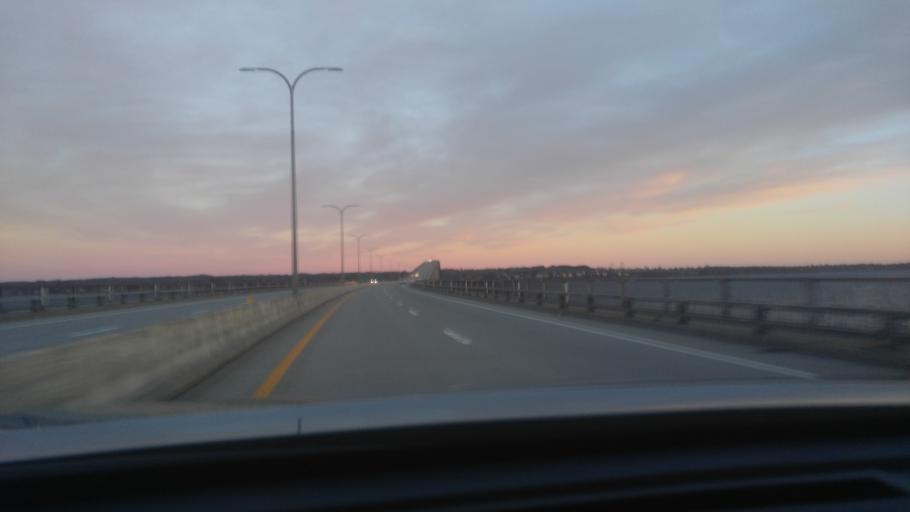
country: US
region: Rhode Island
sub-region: Washington County
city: North Kingstown
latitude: 41.5302
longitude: -71.4144
